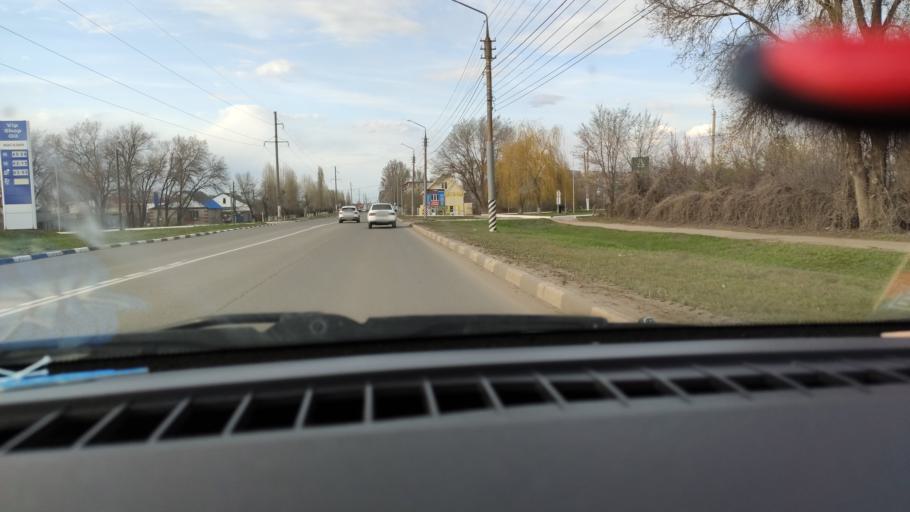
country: RU
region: Saratov
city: Privolzhskiy
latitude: 51.4035
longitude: 46.0378
